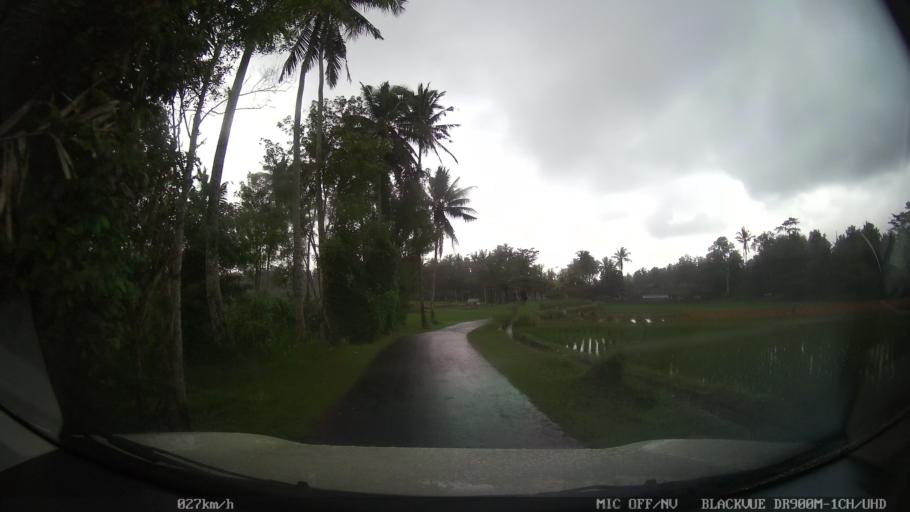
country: ID
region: Bali
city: Kekeran
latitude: -8.4874
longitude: 115.1874
